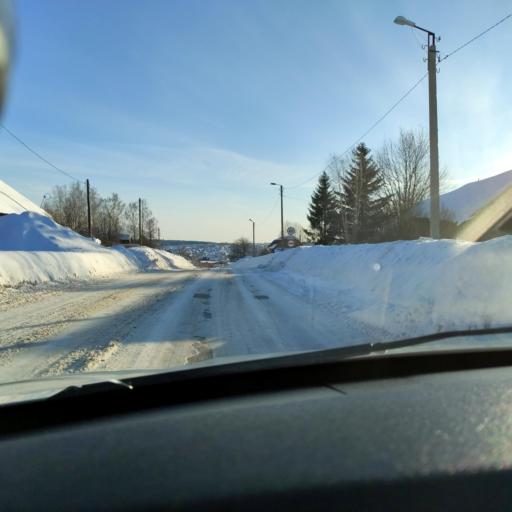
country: RU
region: Perm
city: Polazna
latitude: 58.3162
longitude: 56.4315
